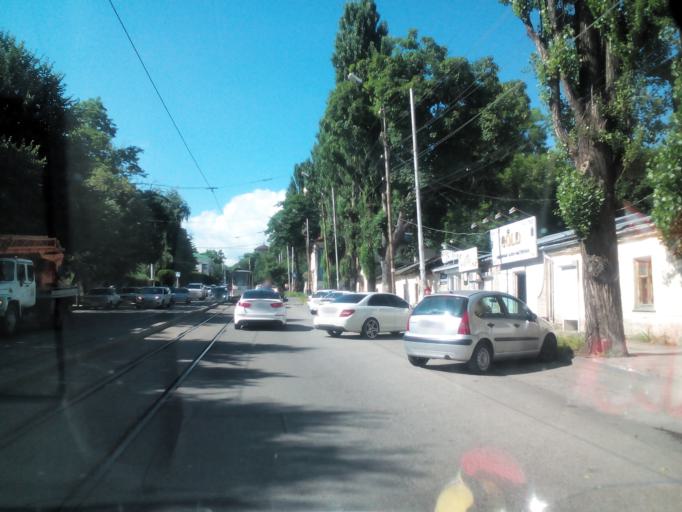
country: RU
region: Stavropol'skiy
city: Pyatigorsk
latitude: 44.0432
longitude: 43.0642
